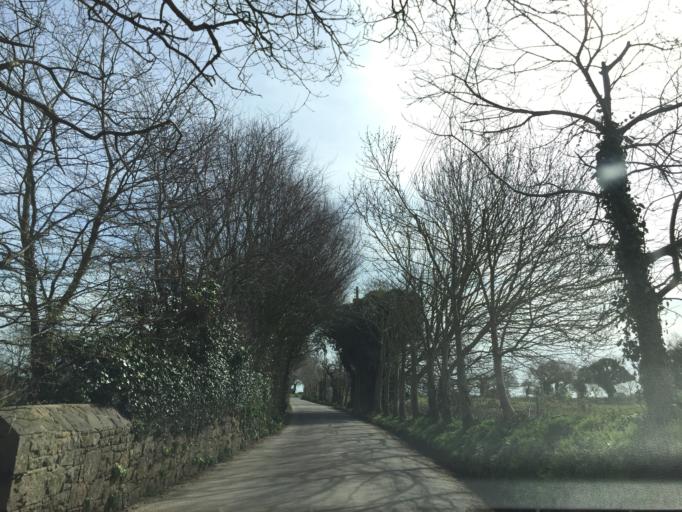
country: JE
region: St Helier
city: Saint Helier
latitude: 49.2287
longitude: -2.0376
